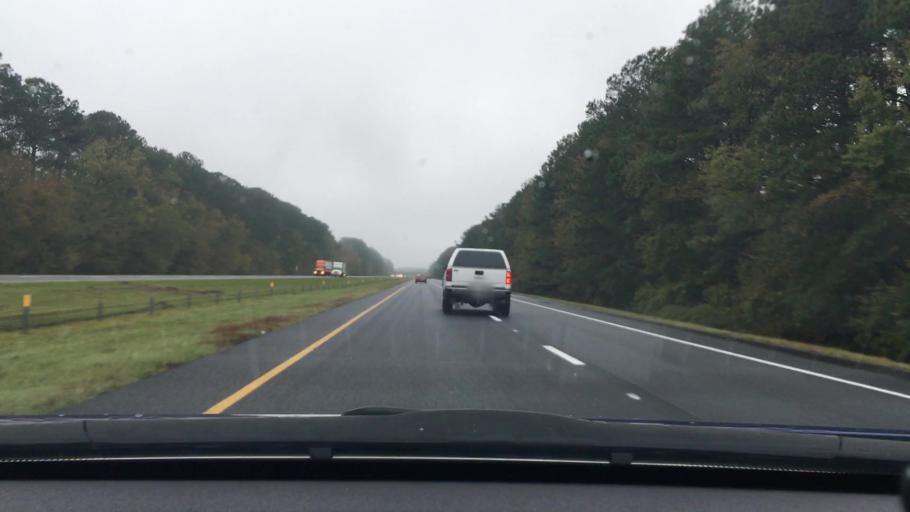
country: US
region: South Carolina
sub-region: Lee County
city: Bishopville
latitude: 34.1955
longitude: -80.1229
